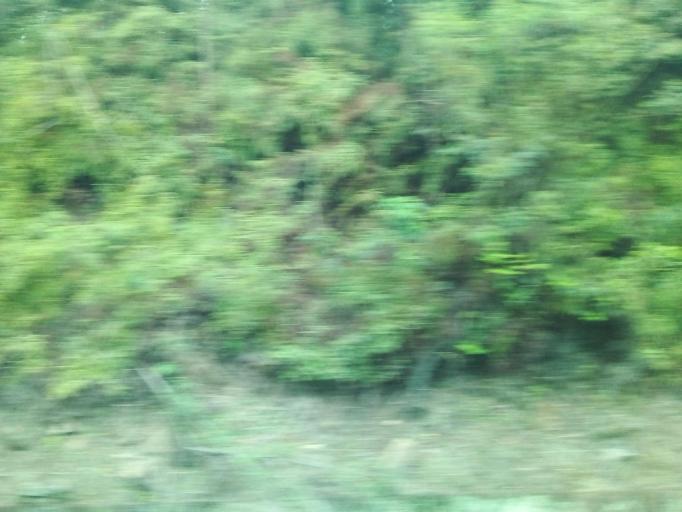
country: BR
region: Minas Gerais
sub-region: Rio Piracicaba
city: Rio Piracicaba
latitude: -19.9728
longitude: -43.2348
